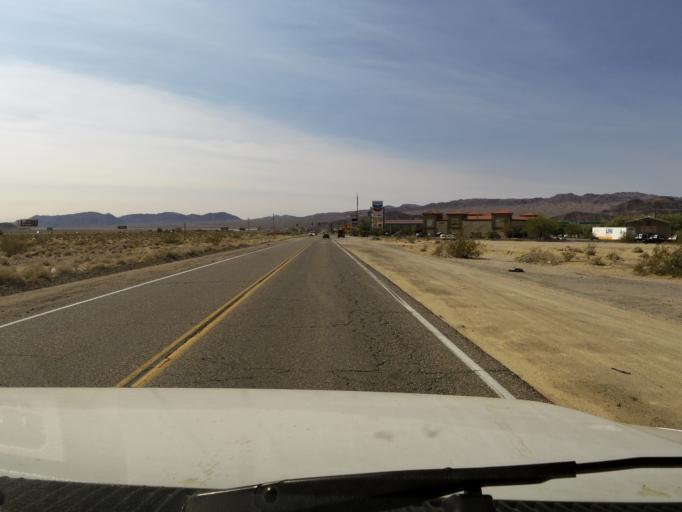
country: US
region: California
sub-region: San Bernardino County
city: Fort Irwin
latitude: 35.2780
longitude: -116.0551
